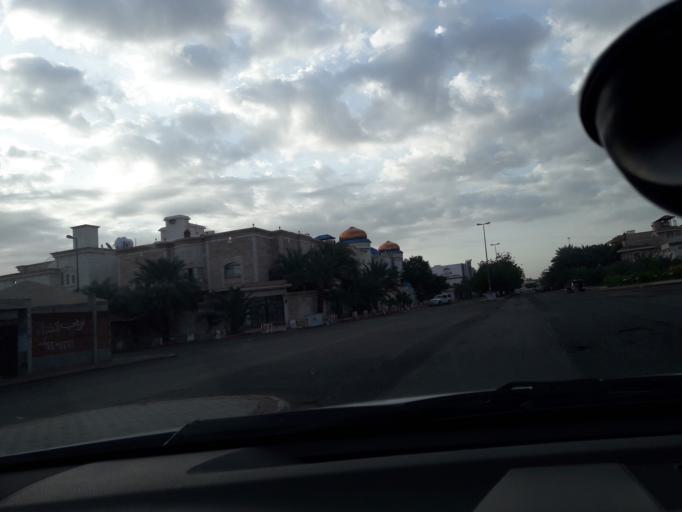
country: SA
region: Al Madinah al Munawwarah
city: Medina
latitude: 24.4246
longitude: 39.6270
